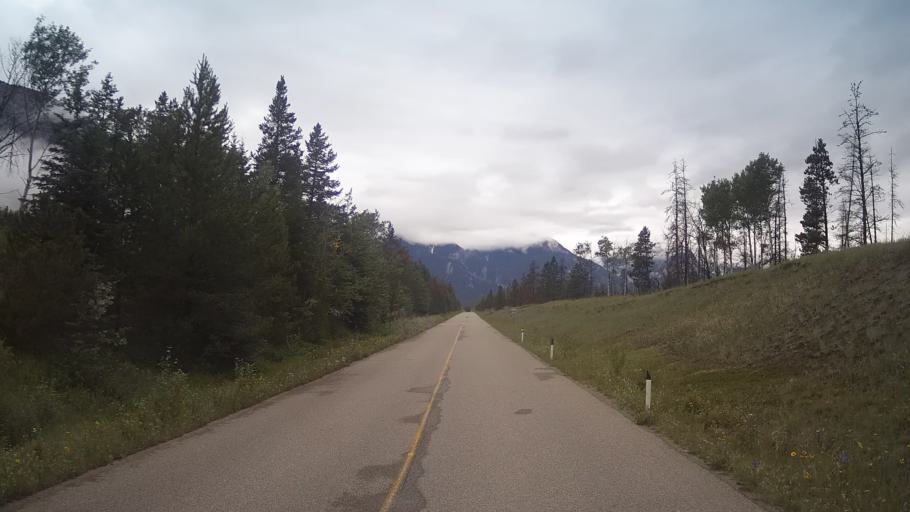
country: CA
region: Alberta
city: Jasper Park Lodge
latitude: 52.9731
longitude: -118.0614
